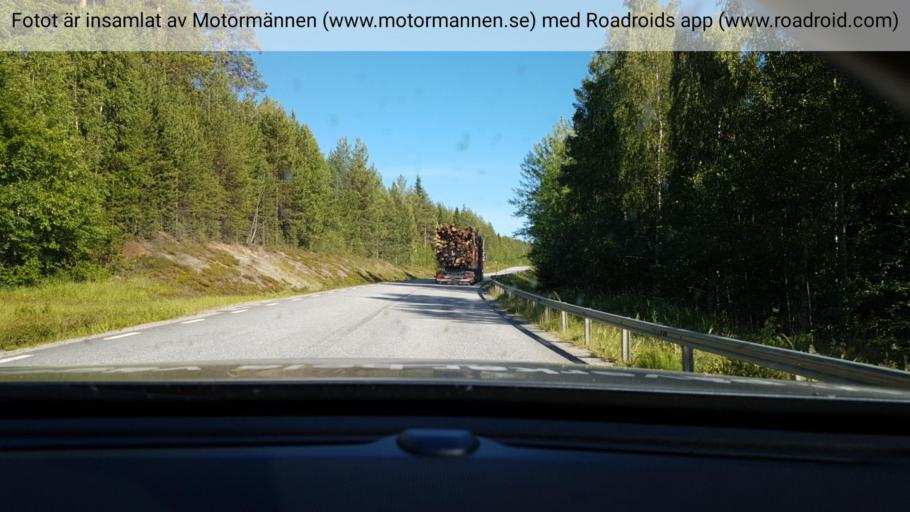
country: SE
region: Vaesterbotten
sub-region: Bjurholms Kommun
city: Bjurholm
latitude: 64.2787
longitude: 19.2465
